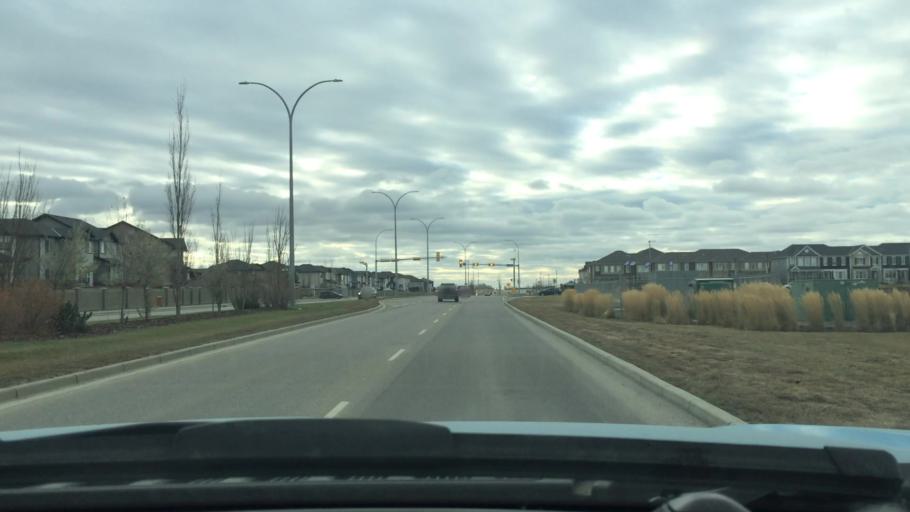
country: CA
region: Alberta
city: Airdrie
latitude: 51.2547
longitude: -114.0251
